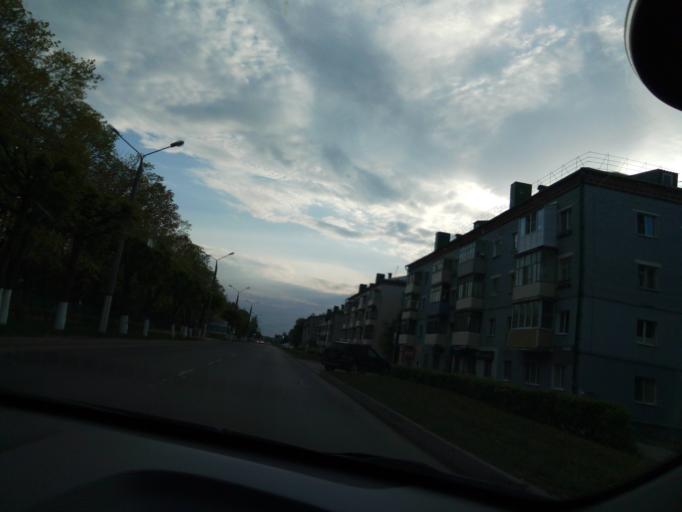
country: RU
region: Chuvashia
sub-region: Cheboksarskiy Rayon
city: Cheboksary
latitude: 56.1200
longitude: 47.2639
